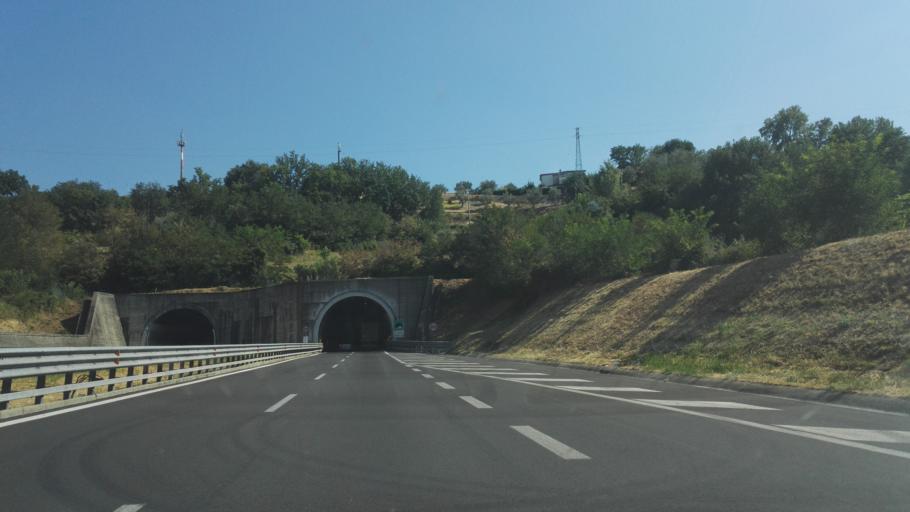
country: IT
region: Calabria
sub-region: Provincia di Cosenza
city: Rosario
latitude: 39.2964
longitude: 16.2370
